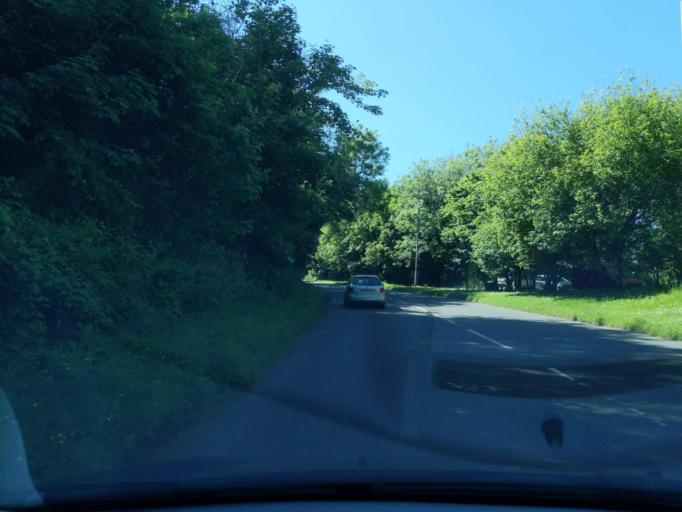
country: GB
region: England
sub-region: Cornwall
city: Helston
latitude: 50.1037
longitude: -5.2835
